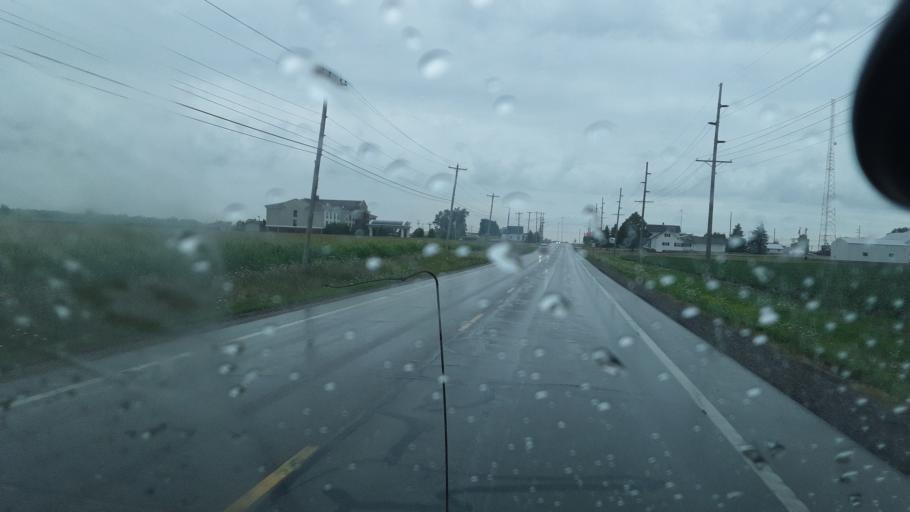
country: US
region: Ohio
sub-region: Williams County
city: Montpelier
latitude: 41.6042
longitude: -84.5558
